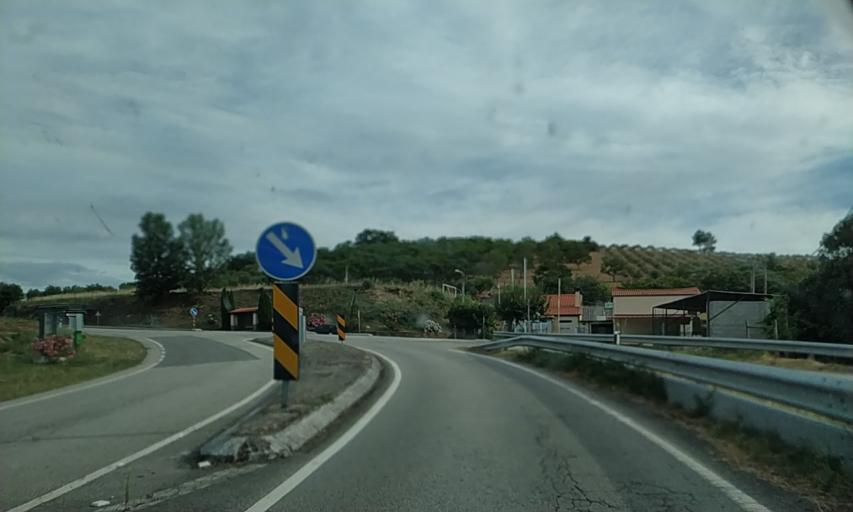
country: PT
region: Viseu
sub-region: Penedono
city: Penedono
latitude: 41.0666
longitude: -7.4031
